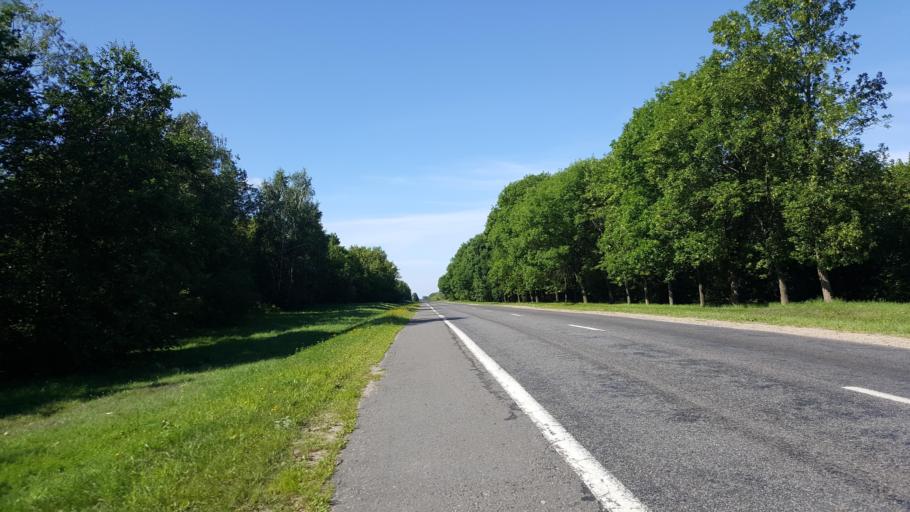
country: BY
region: Brest
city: Kamyanyets
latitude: 52.3850
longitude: 23.8141
